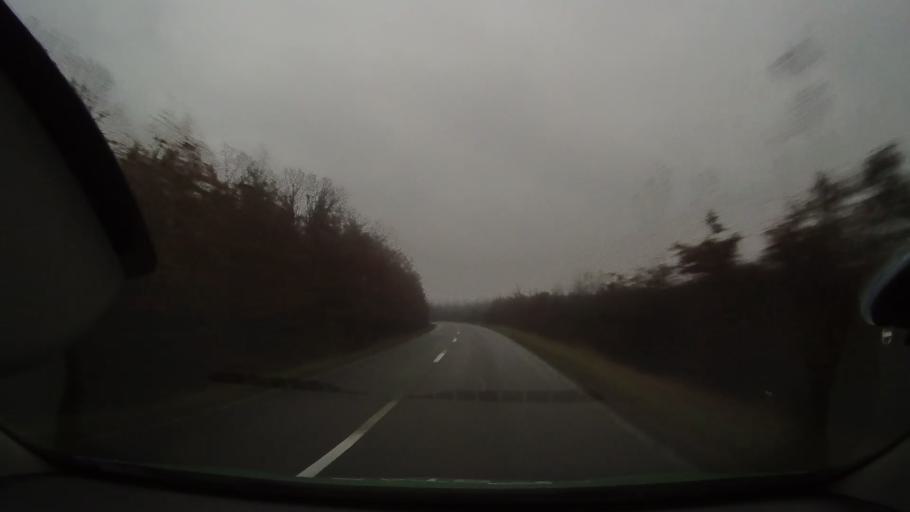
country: RO
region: Arad
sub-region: Comuna Beliu
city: Beliu
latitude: 46.5173
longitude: 21.9560
